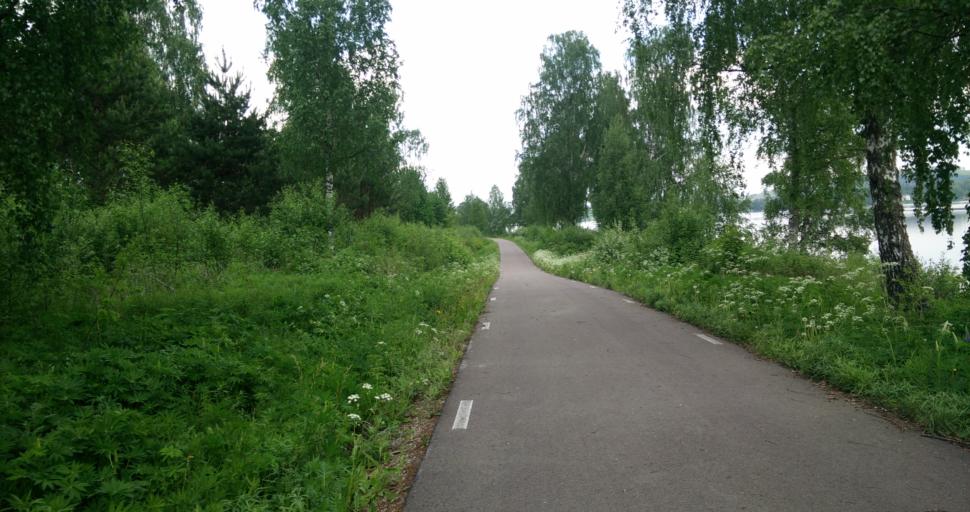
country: SE
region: Vaermland
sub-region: Hagfors Kommun
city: Hagfors
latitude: 60.0005
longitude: 13.6048
